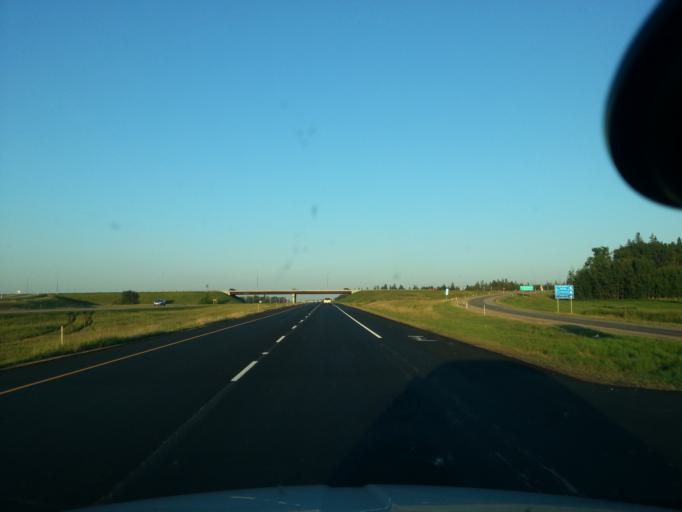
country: CA
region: Alberta
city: Spruce Grove
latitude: 53.5703
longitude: -113.8152
